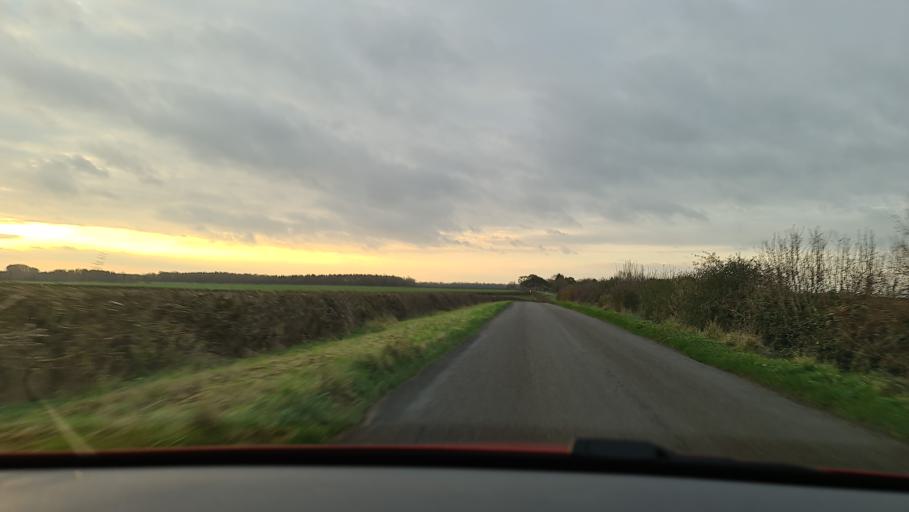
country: GB
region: England
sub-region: Oxfordshire
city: Somerton
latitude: 51.9123
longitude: -1.2755
